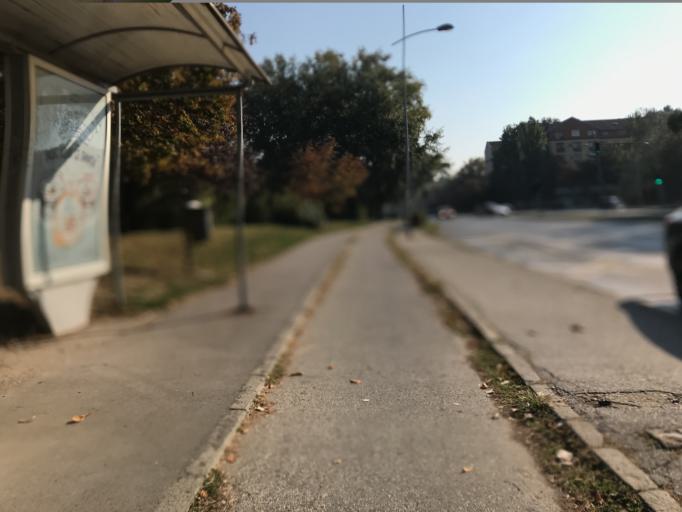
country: RS
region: Autonomna Pokrajina Vojvodina
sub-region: Juznobacki Okrug
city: Novi Sad
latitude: 45.2641
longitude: 19.8230
